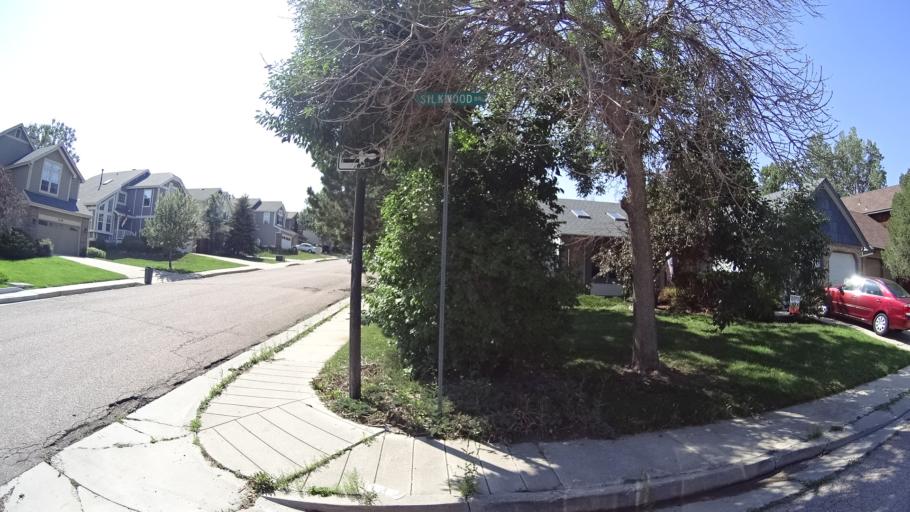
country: US
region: Colorado
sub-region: El Paso County
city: Air Force Academy
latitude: 38.9486
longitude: -104.7884
